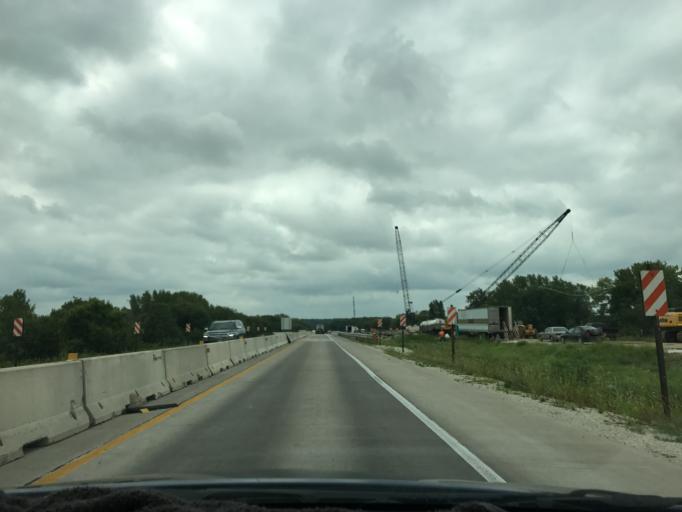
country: US
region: Illinois
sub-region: Henry County
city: Colona
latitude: 41.5214
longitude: -90.3414
